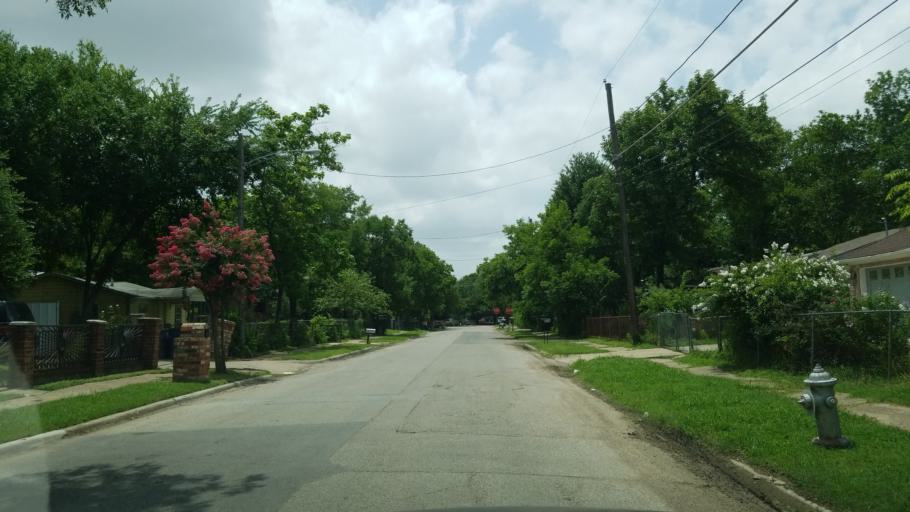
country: US
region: Texas
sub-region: Dallas County
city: Cockrell Hill
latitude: 32.7860
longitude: -96.9003
